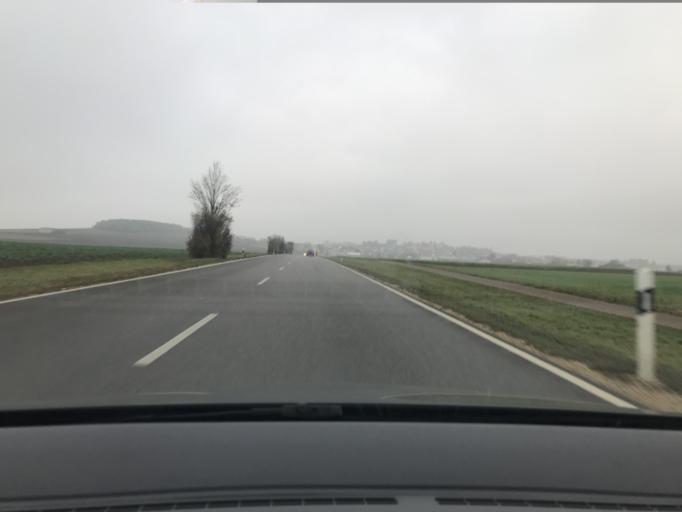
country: DE
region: Bavaria
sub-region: Swabia
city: Wallerstein
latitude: 48.9121
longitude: 10.4673
